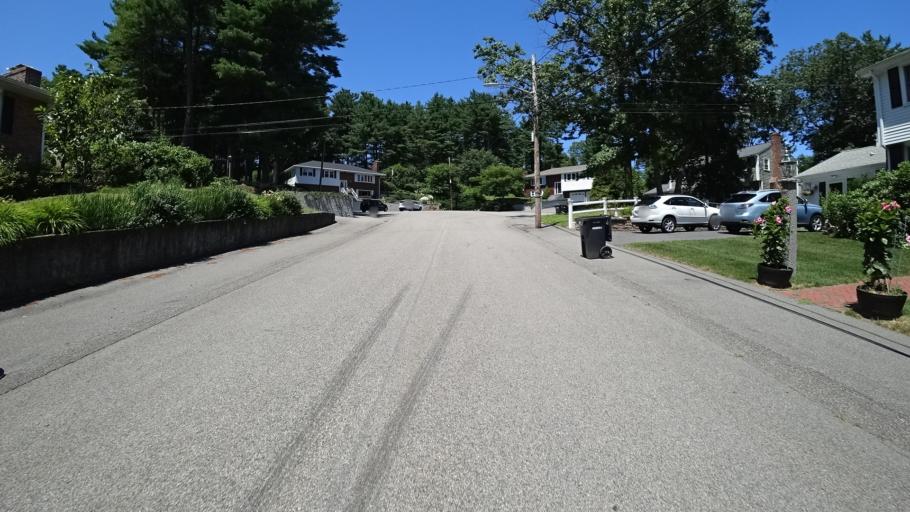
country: US
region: Massachusetts
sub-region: Norfolk County
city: Dedham
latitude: 42.2239
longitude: -71.1535
